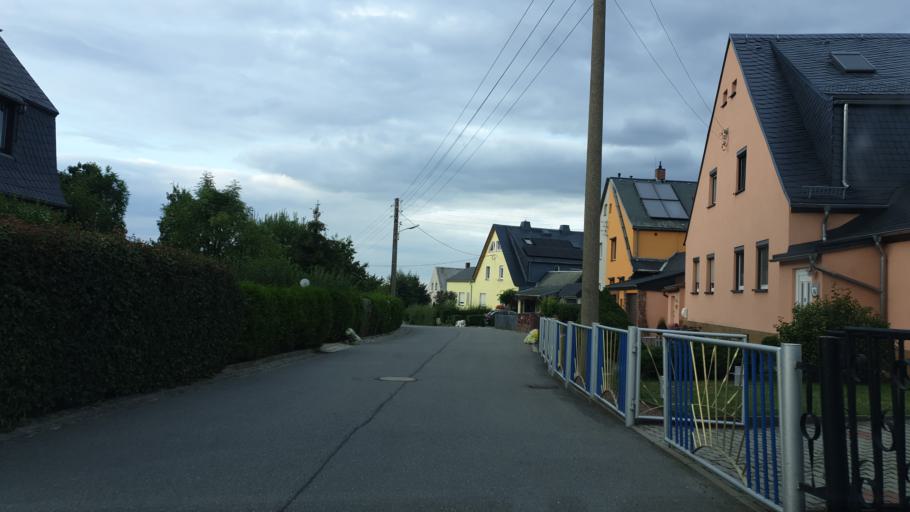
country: DE
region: Saxony
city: Stollberg
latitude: 50.7174
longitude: 12.7664
